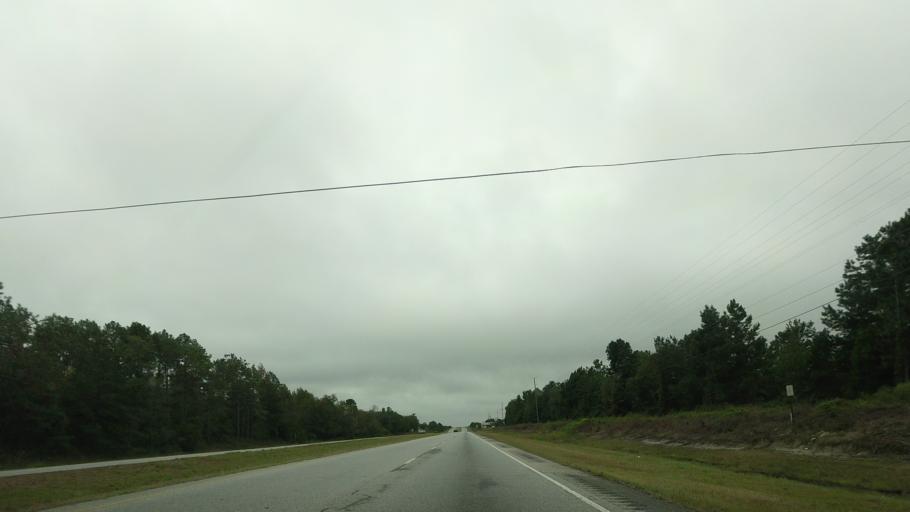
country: US
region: Georgia
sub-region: Lowndes County
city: Valdosta
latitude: 30.8395
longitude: -83.2280
